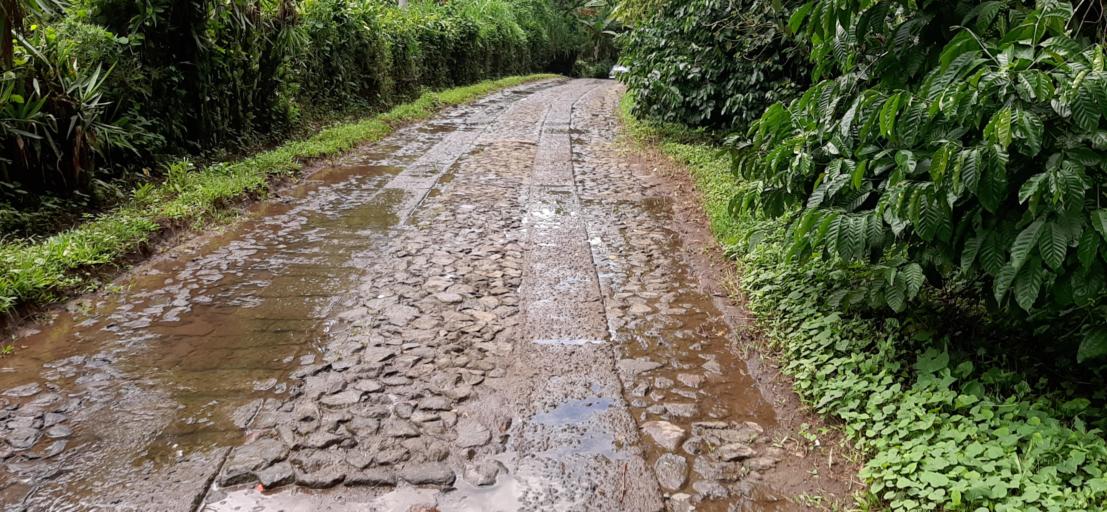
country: GT
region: Retalhuleu
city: San Martin Zapotitlan
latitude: 14.6065
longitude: -91.5745
